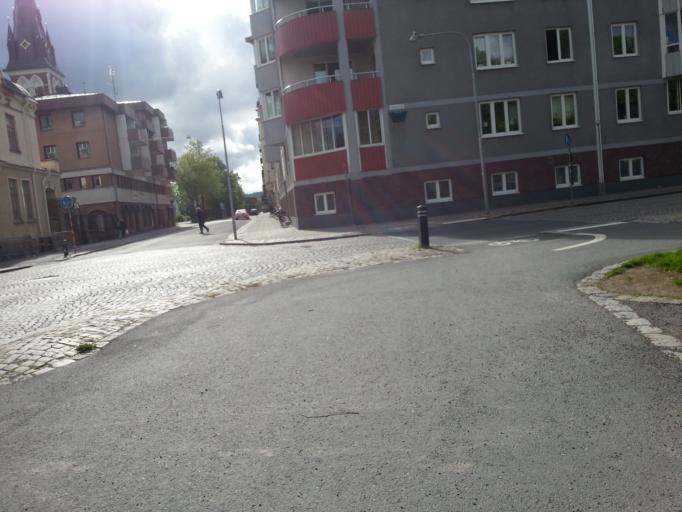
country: SE
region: Joenkoeping
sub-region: Jonkopings Kommun
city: Jonkoping
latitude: 57.7820
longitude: 14.1570
